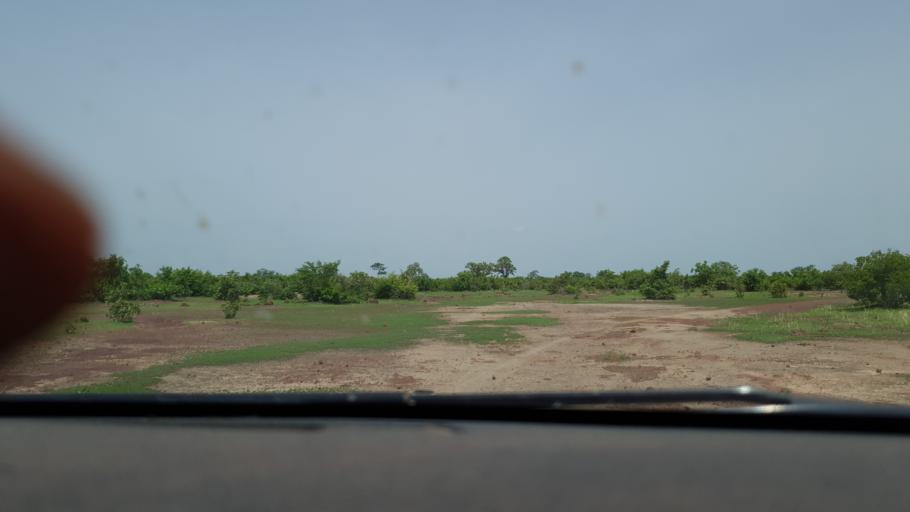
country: ML
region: Koulikoro
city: Koulikoro
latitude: 12.6653
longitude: -7.2269
